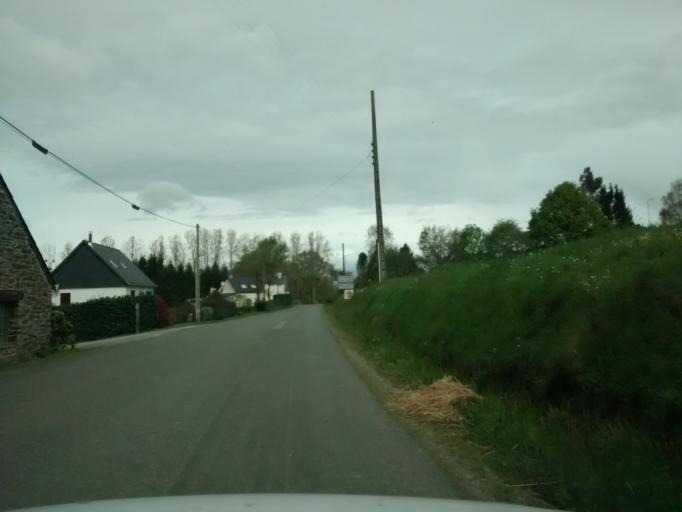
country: FR
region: Brittany
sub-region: Departement du Morbihan
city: Ruffiac
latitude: 47.7903
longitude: -2.3159
